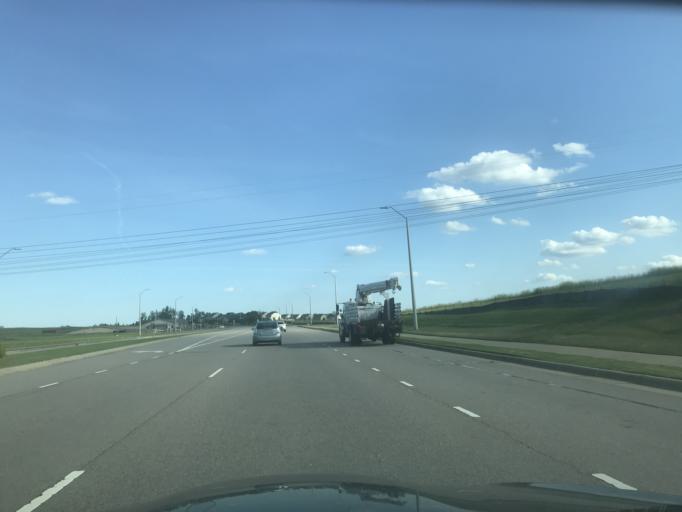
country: US
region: North Carolina
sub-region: Wake County
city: Knightdale
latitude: 35.7781
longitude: -78.4346
